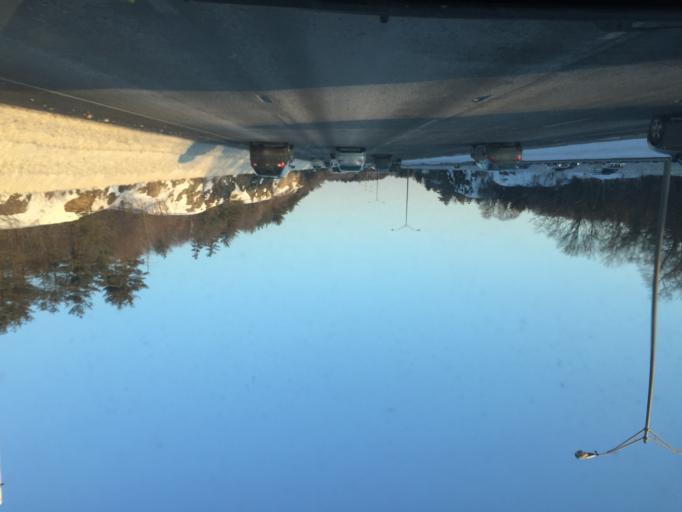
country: US
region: Massachusetts
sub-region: Middlesex County
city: Stoneham
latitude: 42.4519
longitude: -71.1035
